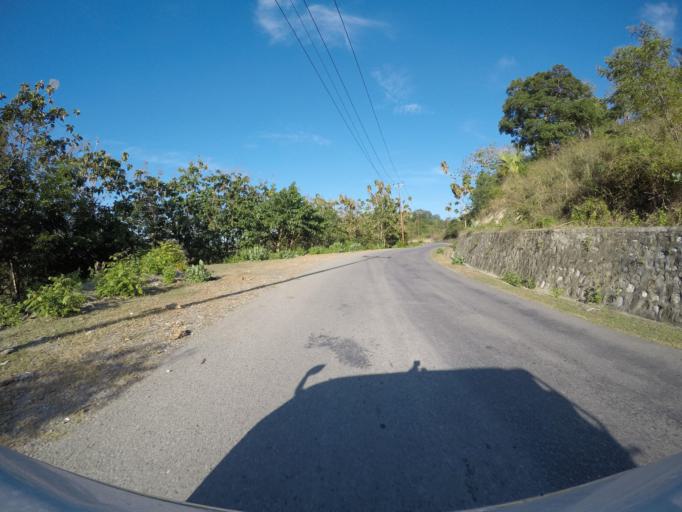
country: TL
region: Viqueque
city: Viqueque
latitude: -8.8725
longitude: 126.3610
